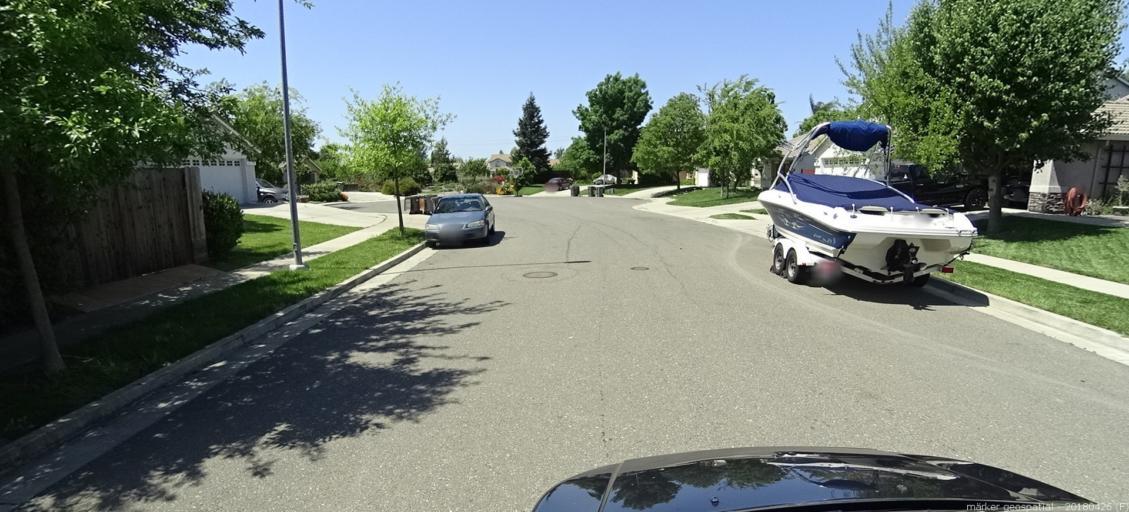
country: US
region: California
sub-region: Yolo County
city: West Sacramento
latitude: 38.5400
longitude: -121.5577
